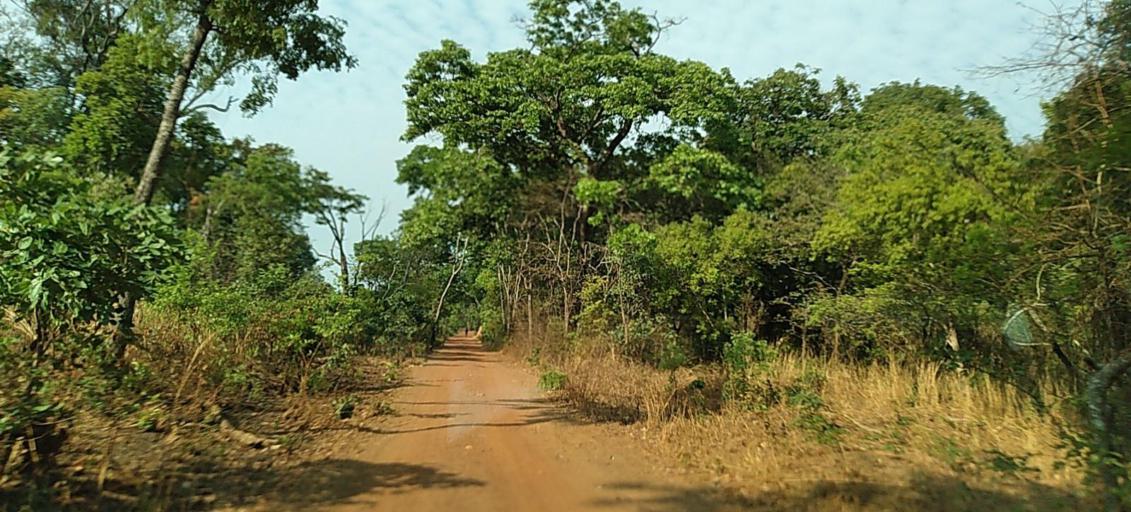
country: ZM
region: Copperbelt
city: Kalulushi
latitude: -12.9928
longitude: 27.7146
